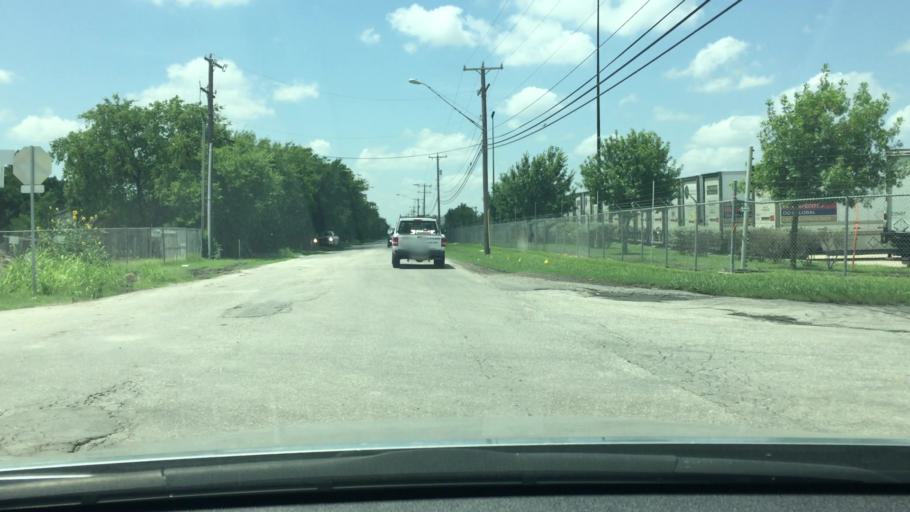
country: US
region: Texas
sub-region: Bexar County
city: Kirby
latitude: 29.4588
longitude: -98.4002
